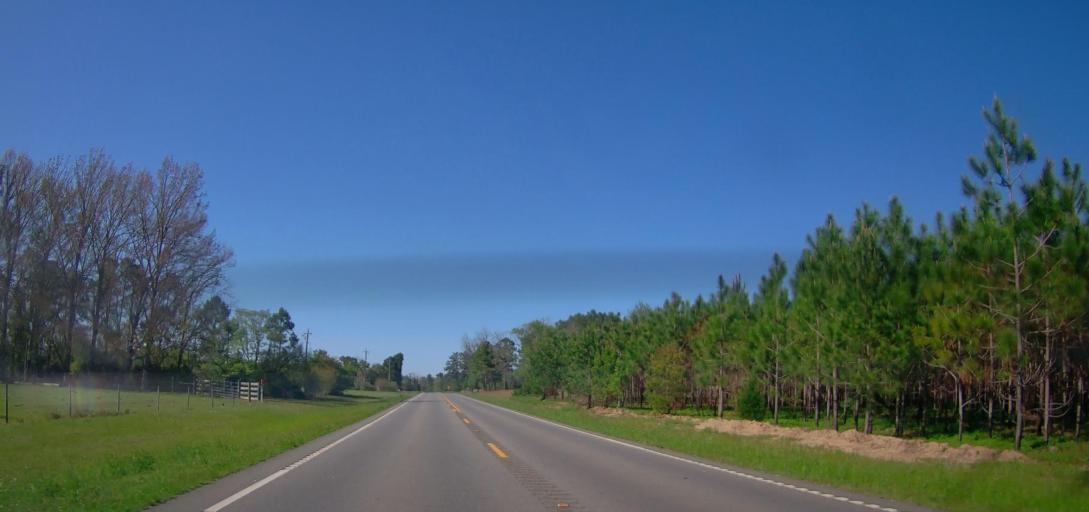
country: US
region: Georgia
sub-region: Pulaski County
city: Hawkinsville
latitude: 32.1239
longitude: -83.5007
